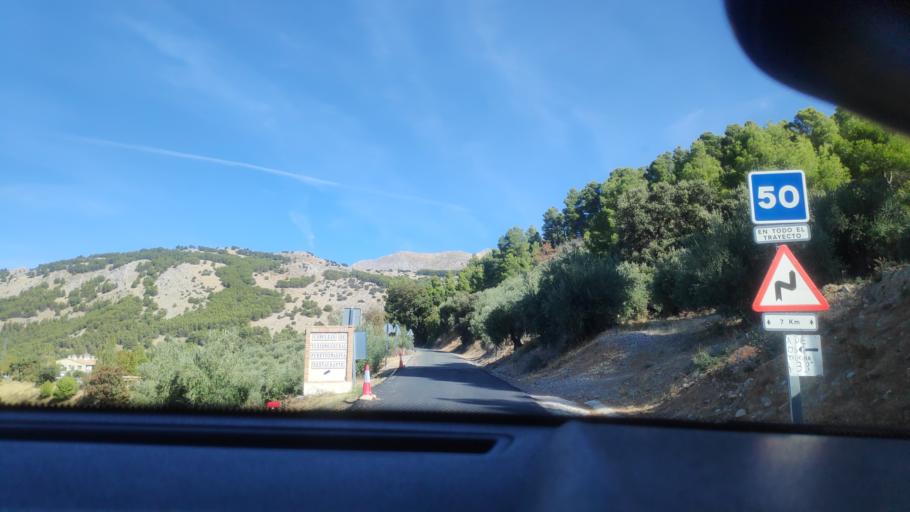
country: ES
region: Andalusia
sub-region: Provincia de Jaen
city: Torres
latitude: 37.7766
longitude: -3.4984
